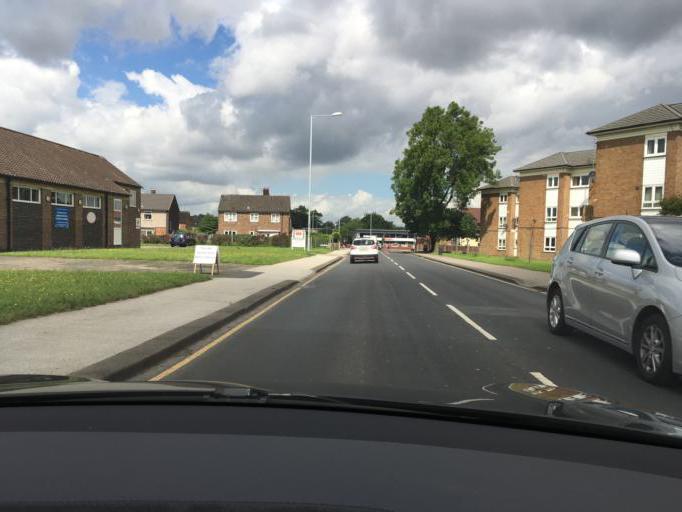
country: GB
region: England
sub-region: Borough of Stockport
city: Cheadle Hulme
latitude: 53.3889
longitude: -2.1906
